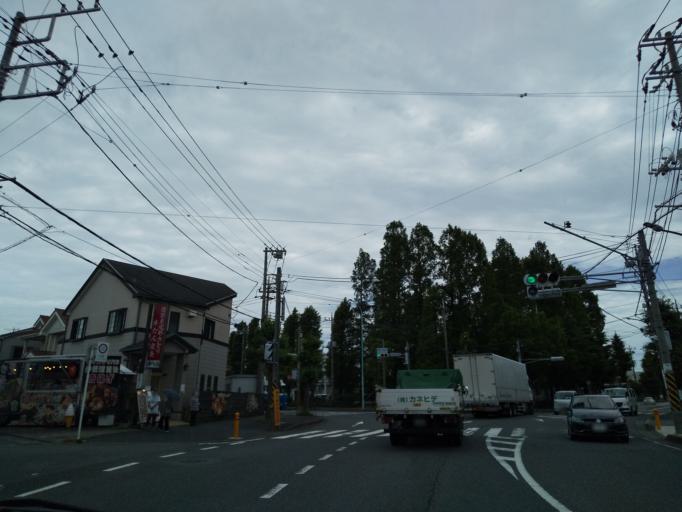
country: JP
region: Kanagawa
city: Zama
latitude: 35.5103
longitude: 139.3583
